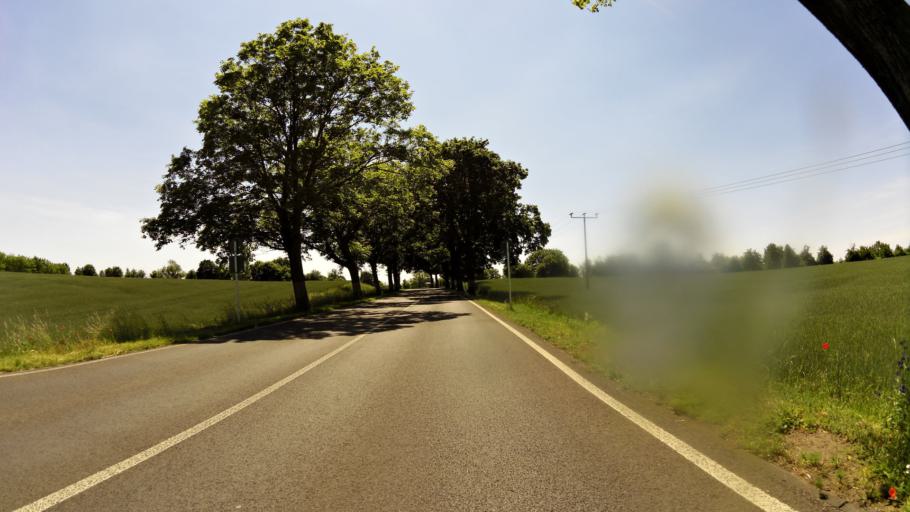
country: DE
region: Brandenburg
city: Lebus
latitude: 52.4025
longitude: 14.5185
